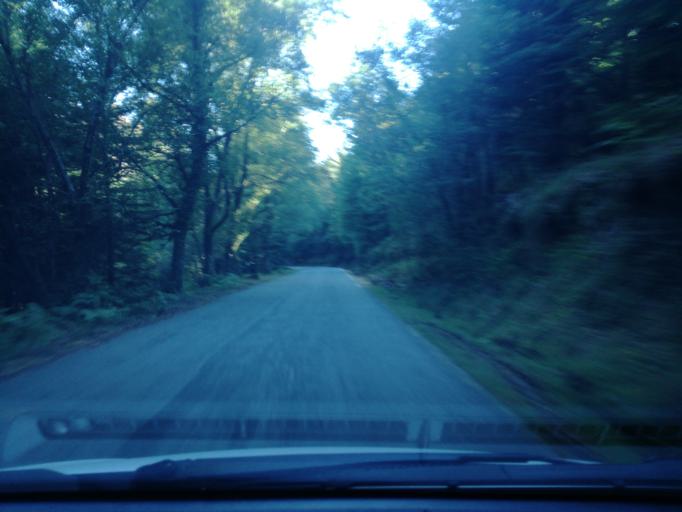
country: ES
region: Galicia
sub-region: Provincia de Ourense
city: Lobios
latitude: 41.7721
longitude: -8.1441
